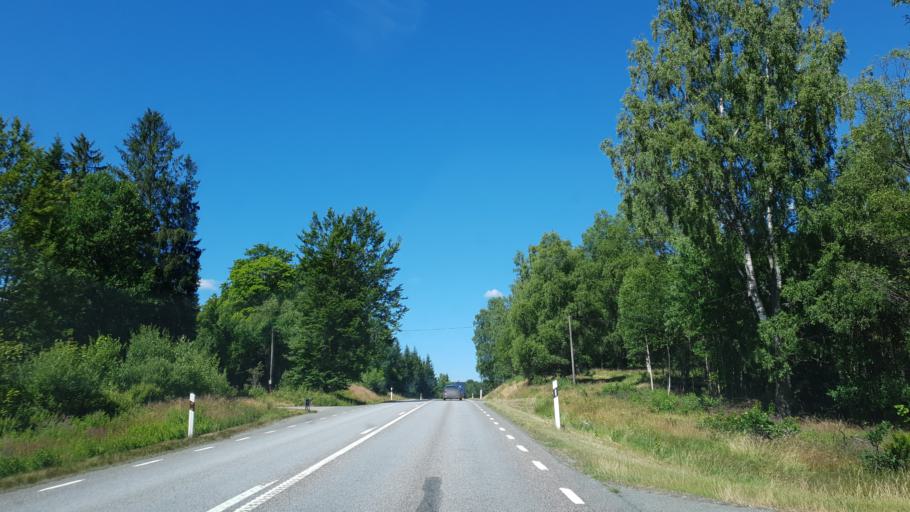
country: SE
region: Joenkoeping
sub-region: Varnamo Kommun
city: Rydaholm
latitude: 56.9388
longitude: 14.3741
